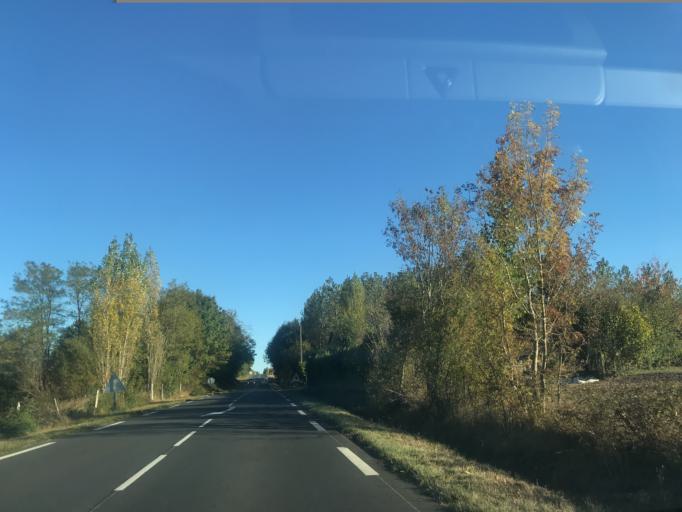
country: FR
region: Poitou-Charentes
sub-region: Departement de la Charente-Maritime
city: Montguyon
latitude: 45.1870
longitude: -0.1344
